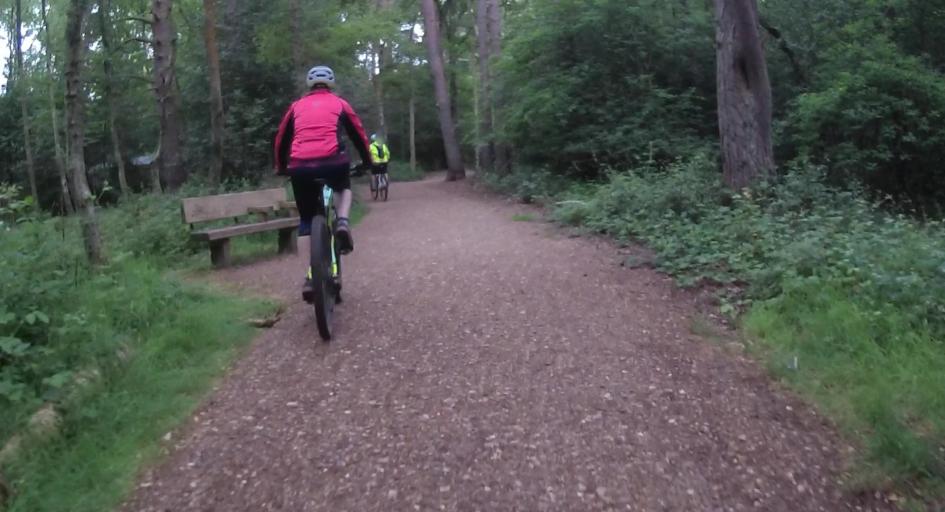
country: GB
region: England
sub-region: Hampshire
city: Farnborough
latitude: 51.2865
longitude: -0.7902
